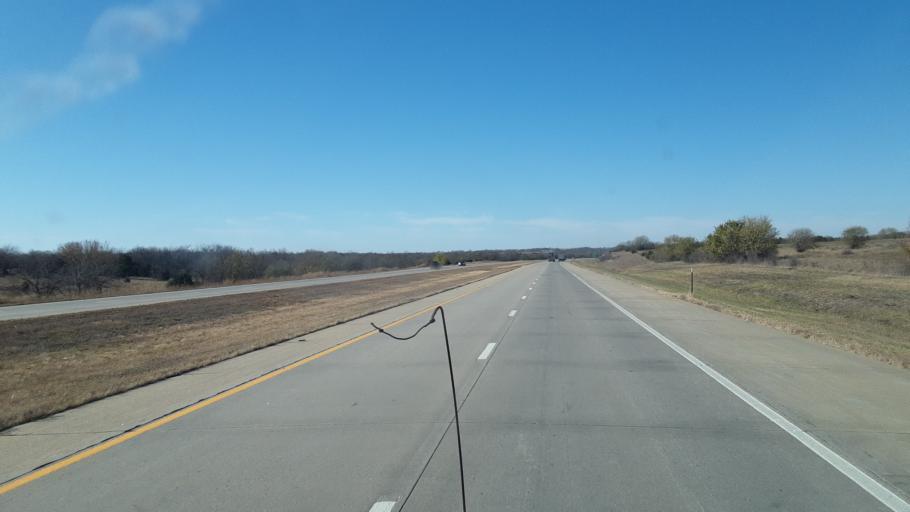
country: US
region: Kansas
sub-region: Osage County
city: Lyndon
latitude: 38.4553
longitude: -95.5667
